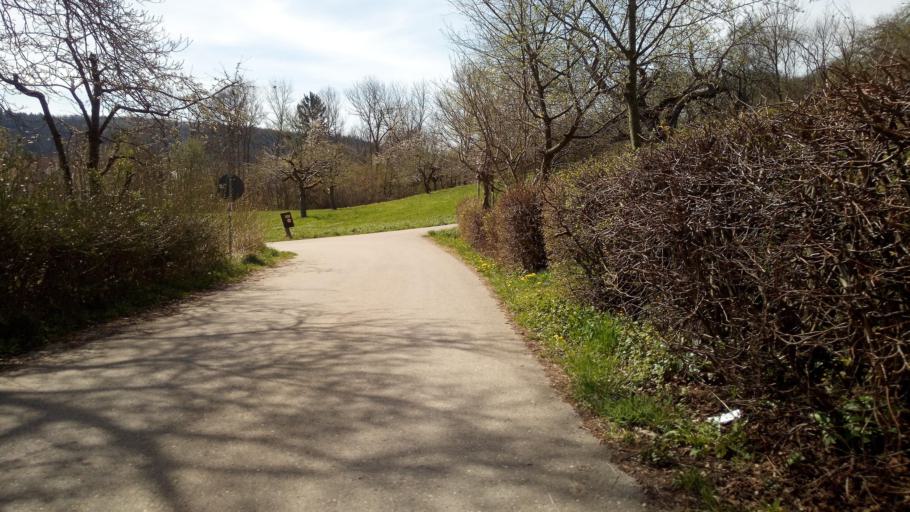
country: DE
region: Baden-Wuerttemberg
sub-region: Regierungsbezirk Stuttgart
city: Donzdorf
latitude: 48.6916
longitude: 9.8109
